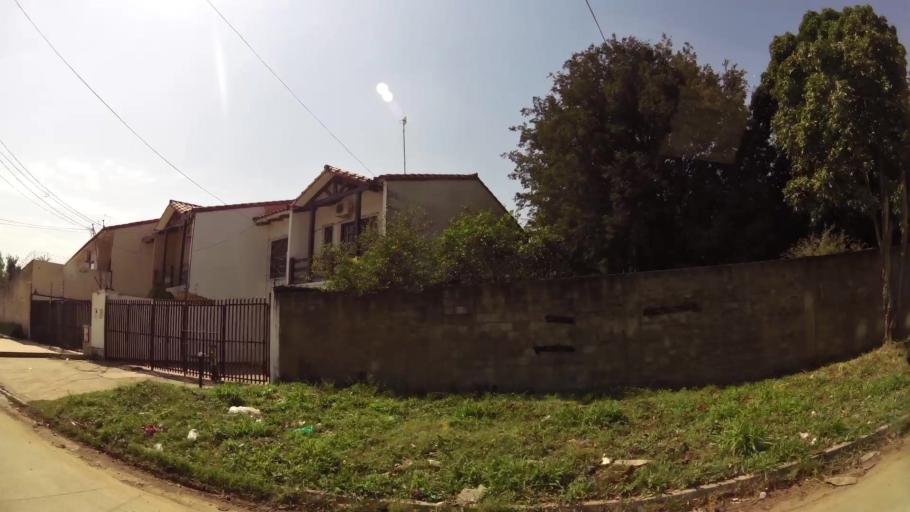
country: BO
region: Santa Cruz
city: Santa Cruz de la Sierra
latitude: -17.7480
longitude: -63.1726
